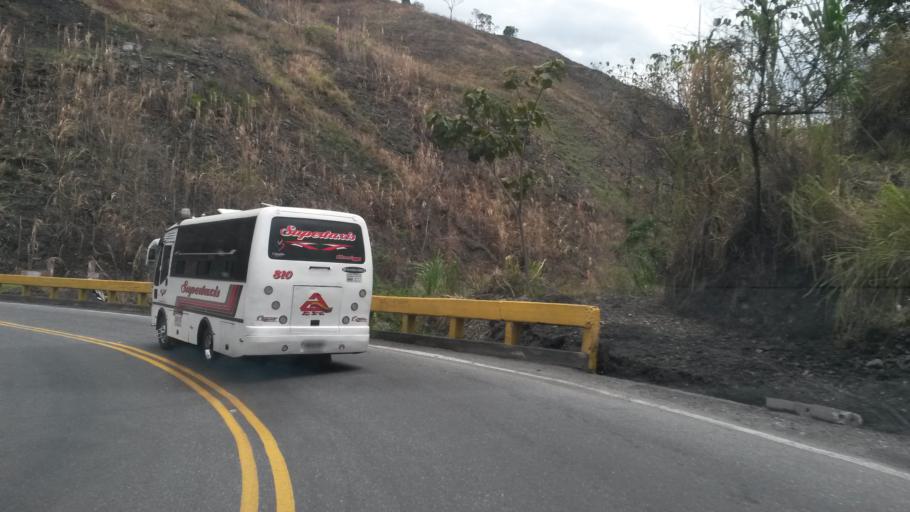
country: CO
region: Cauca
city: Rosas
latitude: 2.2758
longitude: -76.7099
